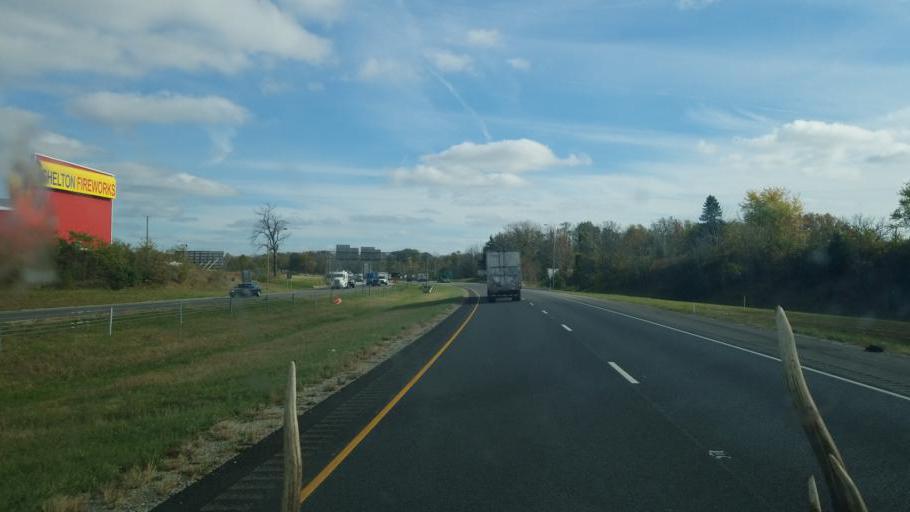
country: US
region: Ohio
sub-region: Preble County
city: New Paris
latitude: 39.8317
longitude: -84.8156
